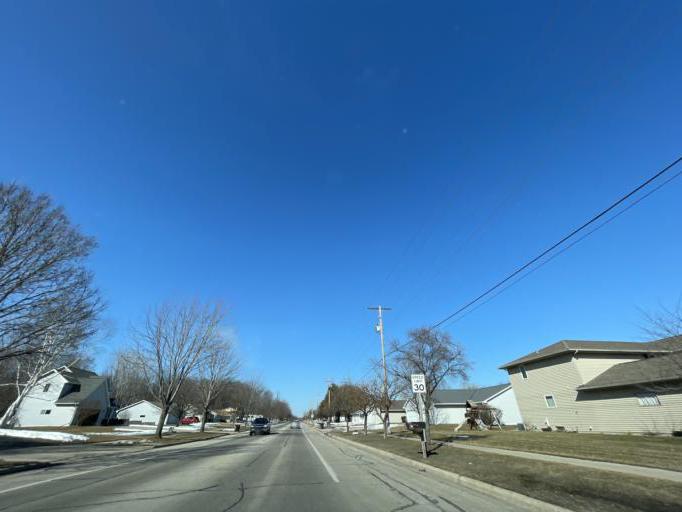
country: US
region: Wisconsin
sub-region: Brown County
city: Howard
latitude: 44.5802
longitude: -88.0845
